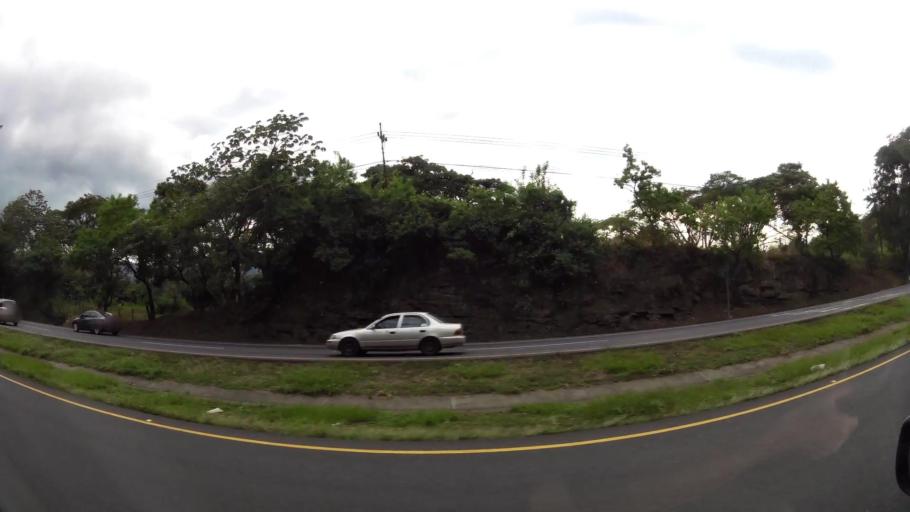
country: CR
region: San Jose
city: Santa Ana
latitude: 9.9478
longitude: -84.1744
